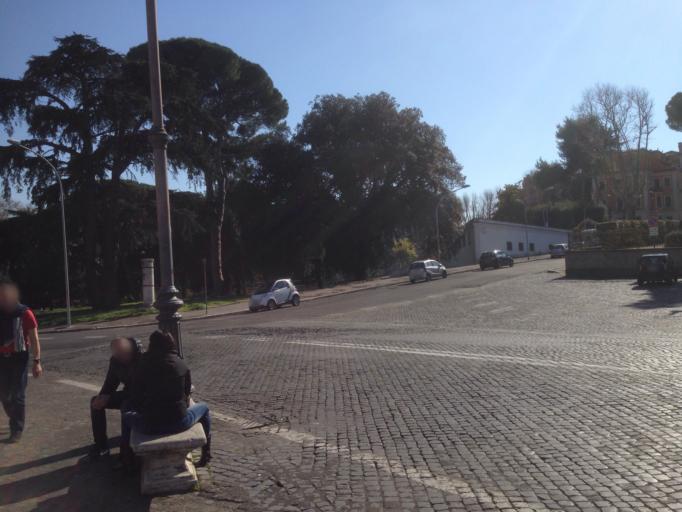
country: VA
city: Vatican City
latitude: 41.8889
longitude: 12.4646
